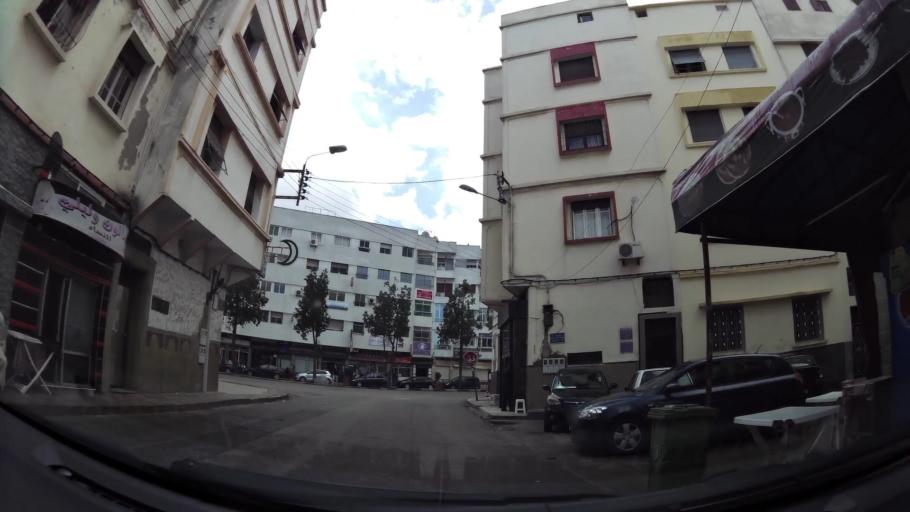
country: MA
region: Grand Casablanca
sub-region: Casablanca
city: Casablanca
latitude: 33.5540
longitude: -7.6039
